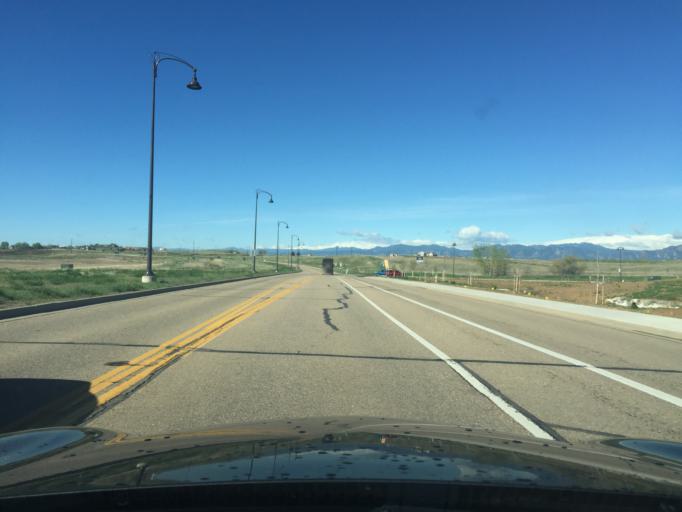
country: US
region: Colorado
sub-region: Boulder County
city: Erie
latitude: 39.9931
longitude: -105.0130
